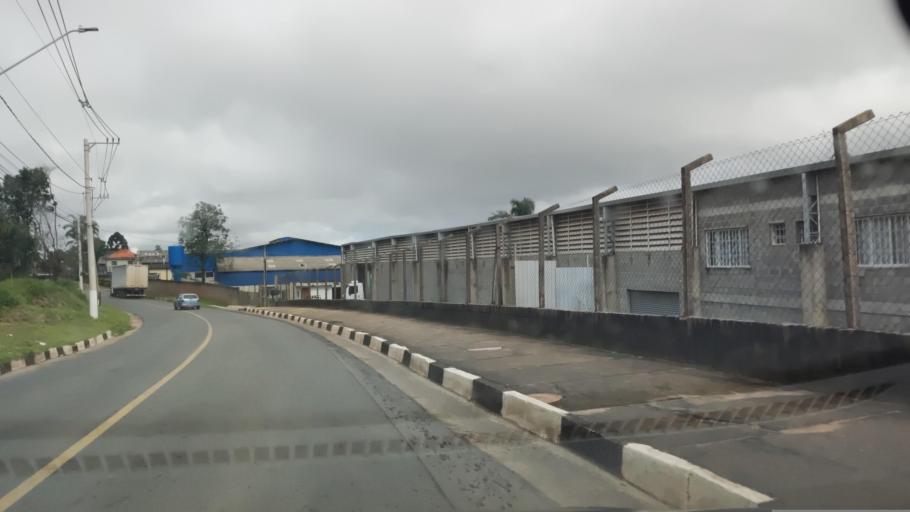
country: BR
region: Sao Paulo
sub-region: Vargem Grande Paulista
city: Vargem Grande Paulista
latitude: -23.6464
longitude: -47.0530
